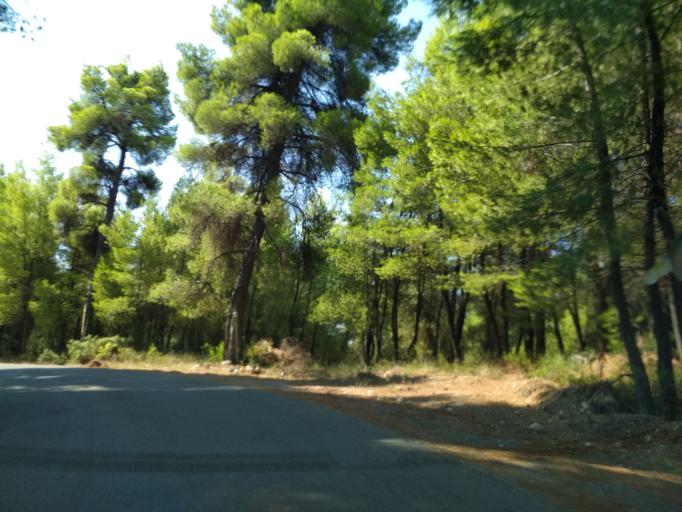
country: GR
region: Central Greece
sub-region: Nomos Evvoias
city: Roviai
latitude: 38.8250
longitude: 23.2666
